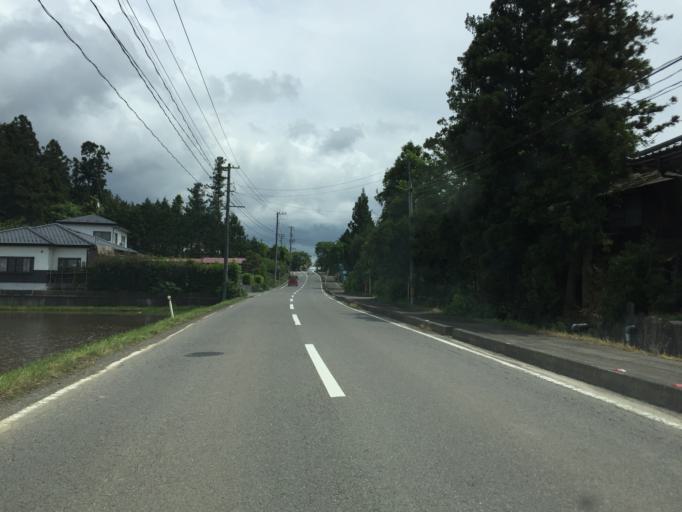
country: JP
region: Fukushima
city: Ishikawa
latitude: 37.1139
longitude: 140.3260
